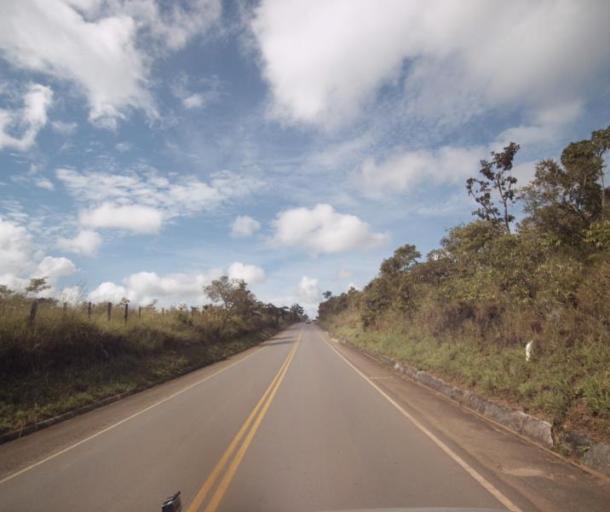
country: BR
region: Goias
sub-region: Pirenopolis
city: Pirenopolis
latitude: -15.8911
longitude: -48.7965
